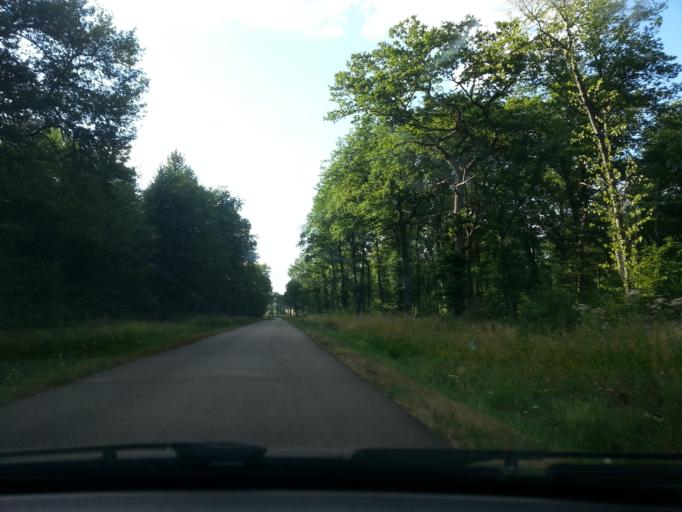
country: FR
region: Bourgogne
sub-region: Departement de Saone-et-Loire
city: Dracy-le-Fort
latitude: 46.7694
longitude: 4.7687
